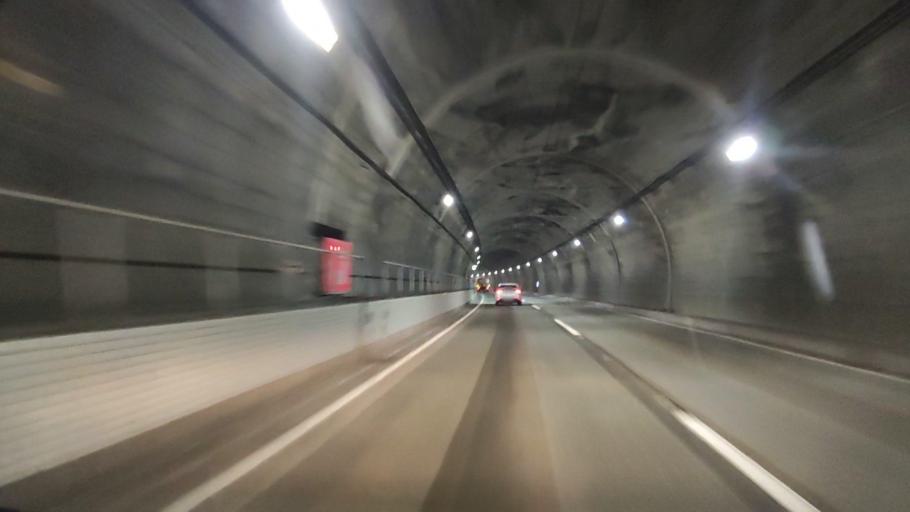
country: JP
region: Iwate
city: Ichinohe
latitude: 40.2353
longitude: 141.3950
